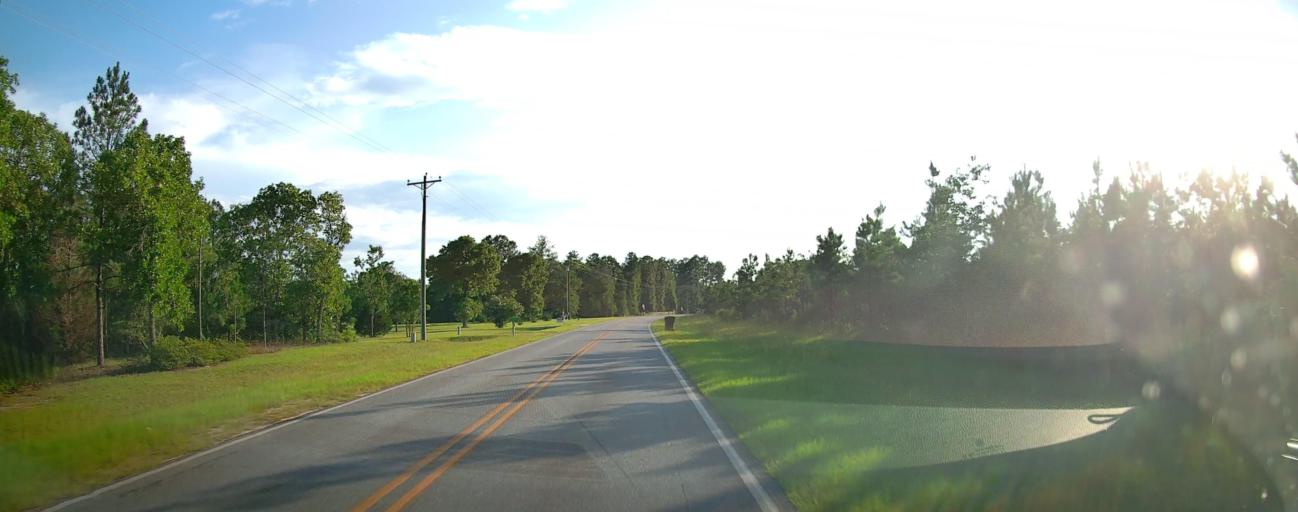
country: US
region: Georgia
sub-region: Peach County
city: Byron
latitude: 32.7072
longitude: -83.8023
